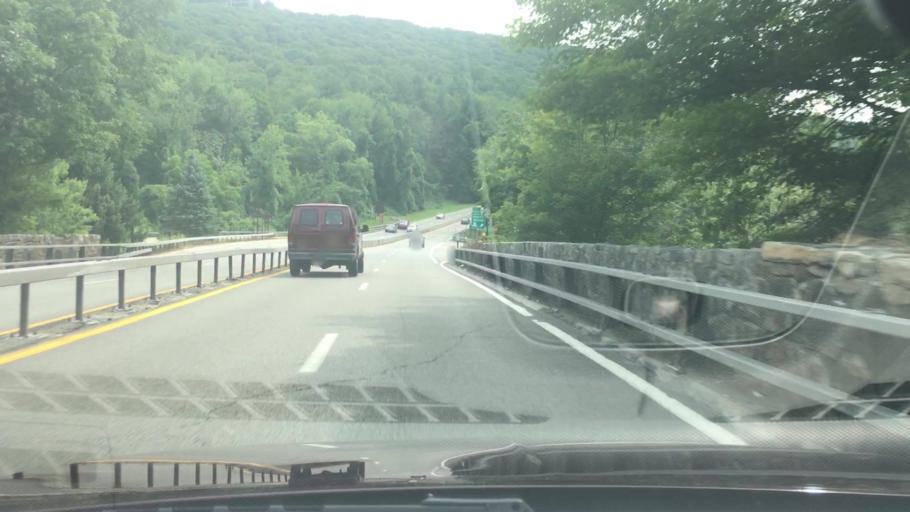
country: US
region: New York
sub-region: Putnam County
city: Mahopac
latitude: 41.4096
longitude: -73.7869
